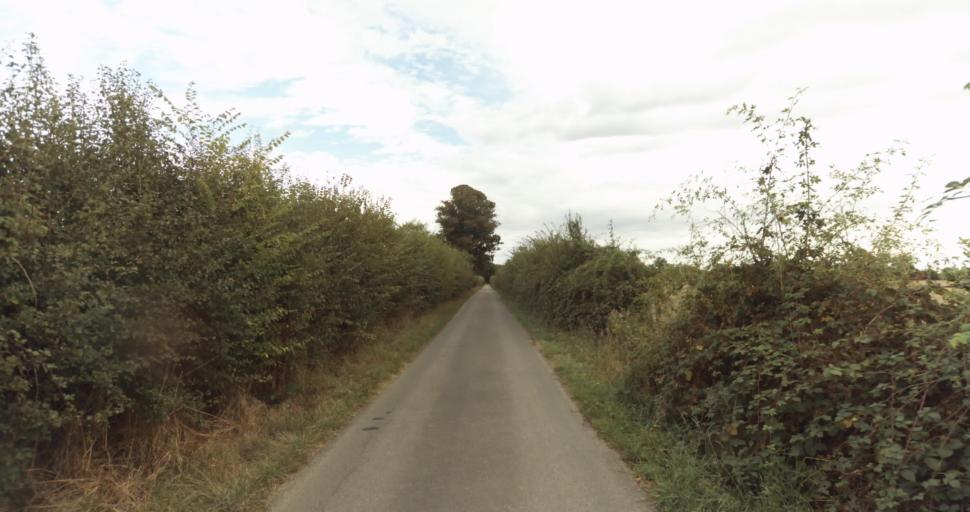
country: FR
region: Lower Normandy
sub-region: Departement du Calvados
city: La Vespiere
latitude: 48.9423
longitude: 0.3321
